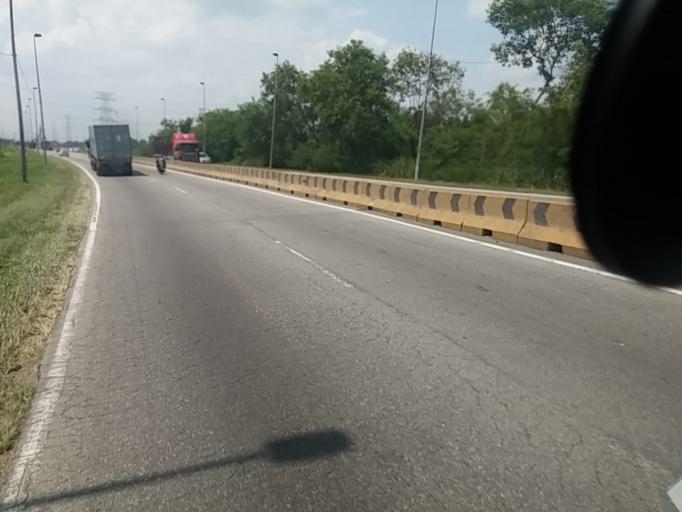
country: MY
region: Selangor
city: Klang
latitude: 2.9650
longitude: 101.3596
